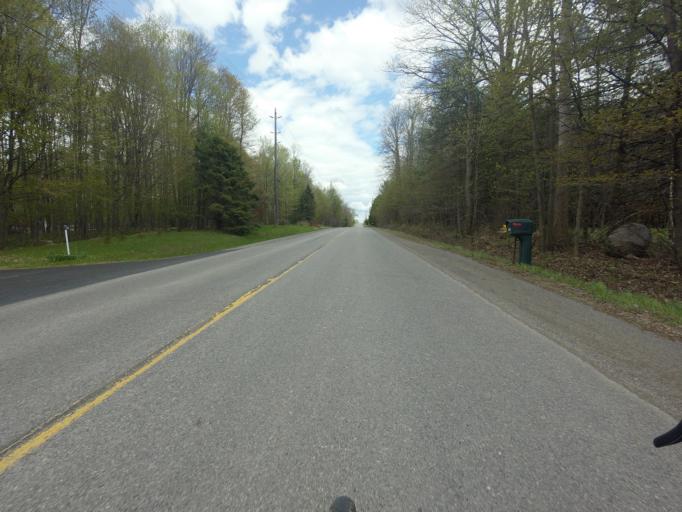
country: CA
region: Ontario
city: Carleton Place
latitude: 45.2285
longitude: -76.2500
